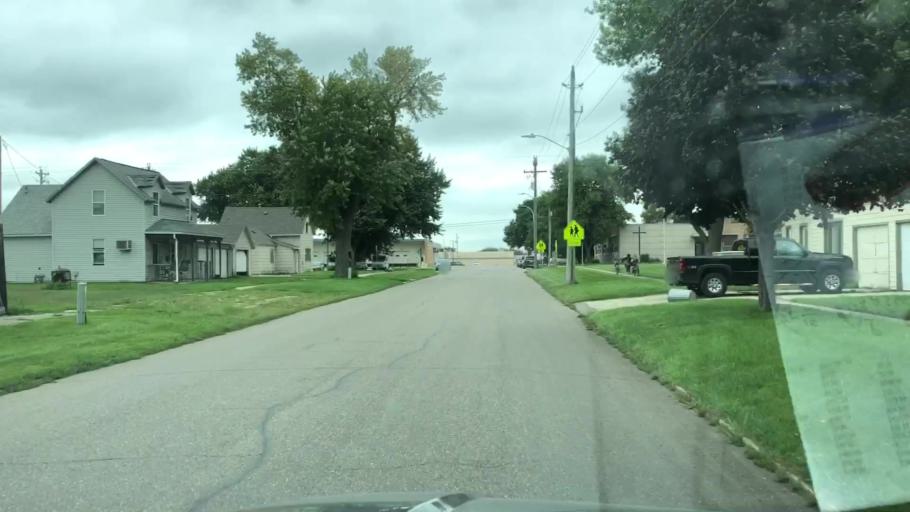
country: US
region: Iowa
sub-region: O'Brien County
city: Sheldon
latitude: 43.1781
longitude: -95.8533
